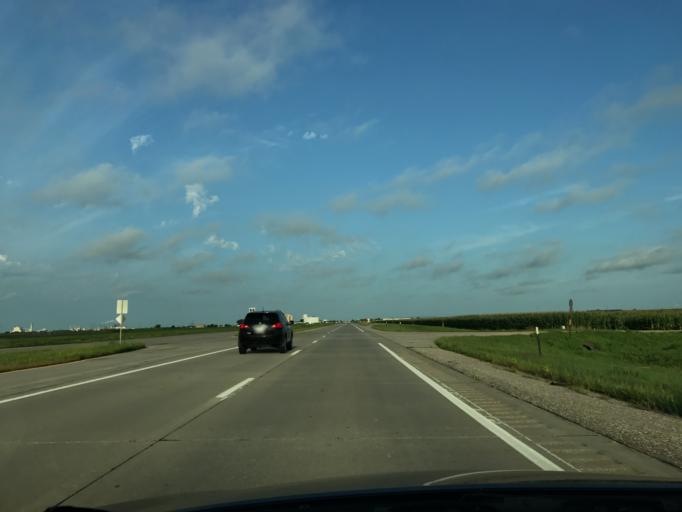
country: US
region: Nebraska
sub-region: Platte County
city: Columbus
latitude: 41.4387
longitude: -97.2322
